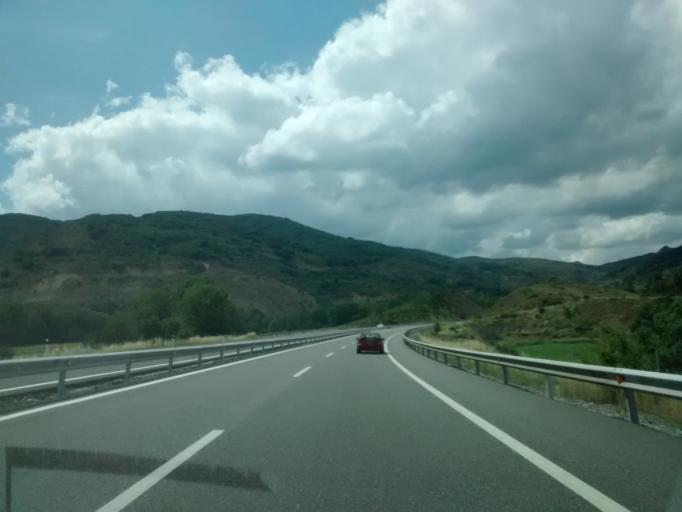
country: ES
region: Castille and Leon
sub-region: Provincia de Leon
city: Soto y Amio
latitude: 42.8248
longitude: -5.8694
